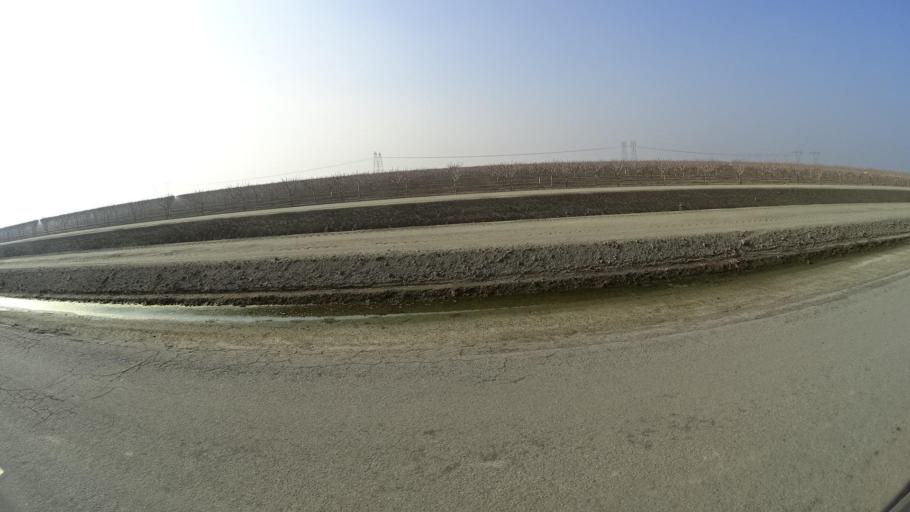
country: US
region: California
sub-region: Kern County
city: Greenfield
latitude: 35.1561
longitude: -119.0393
